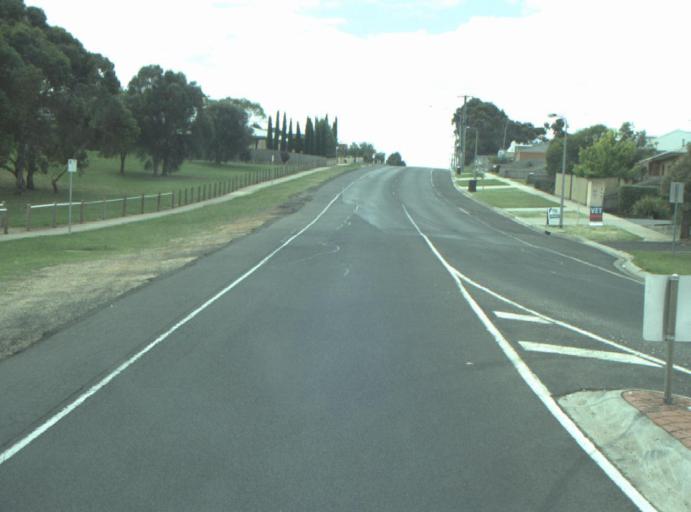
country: AU
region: Victoria
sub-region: Greater Geelong
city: Wandana Heights
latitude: -38.1926
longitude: 144.3148
